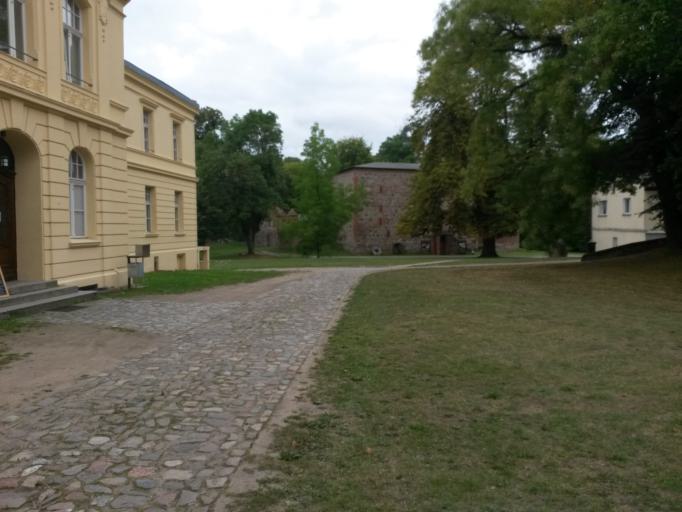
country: DE
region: Brandenburg
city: Gerswalde
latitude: 53.1695
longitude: 13.7473
